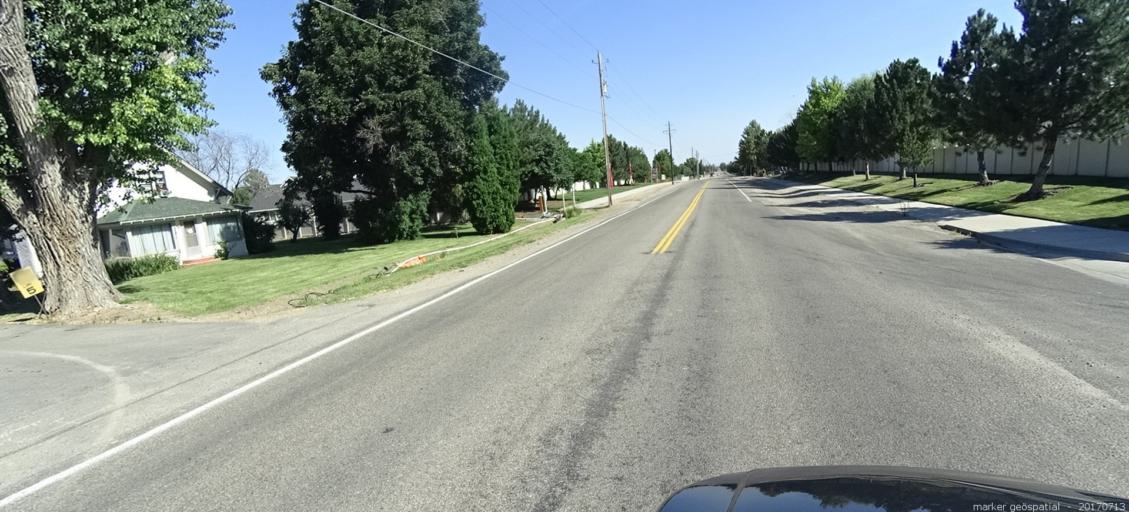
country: US
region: Idaho
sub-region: Ada County
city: Kuna
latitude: 43.5121
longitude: -116.4138
